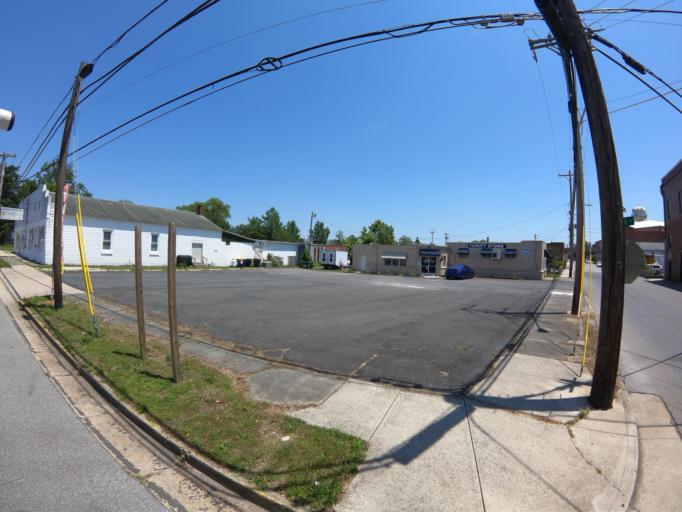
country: US
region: Delaware
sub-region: Sussex County
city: Milford
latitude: 38.9130
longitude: -75.4308
